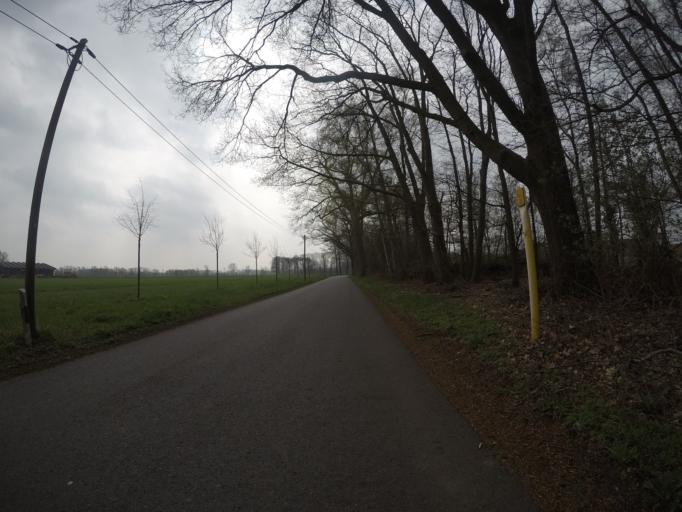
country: DE
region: North Rhine-Westphalia
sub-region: Regierungsbezirk Dusseldorf
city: Bocholt
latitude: 51.8743
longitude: 6.6437
